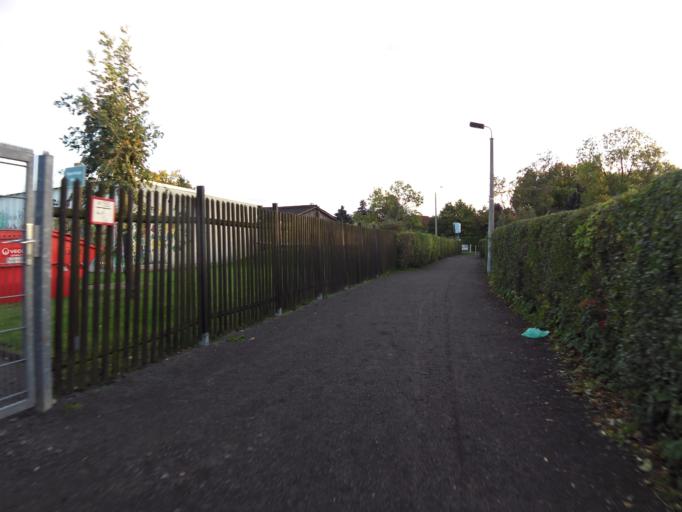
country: DE
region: Saxony
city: Leipzig
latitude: 51.3188
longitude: 12.4324
